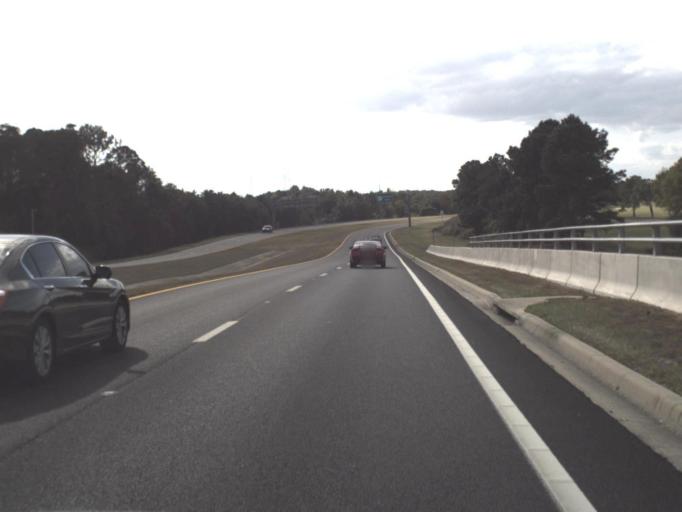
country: US
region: Florida
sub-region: Osceola County
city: Celebration
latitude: 28.3394
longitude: -81.4966
